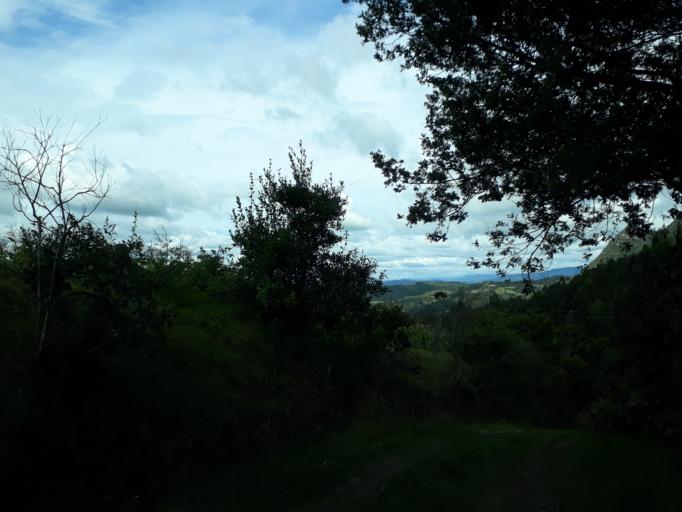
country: CO
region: Cundinamarca
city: Simijaca
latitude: 5.4787
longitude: -73.8870
